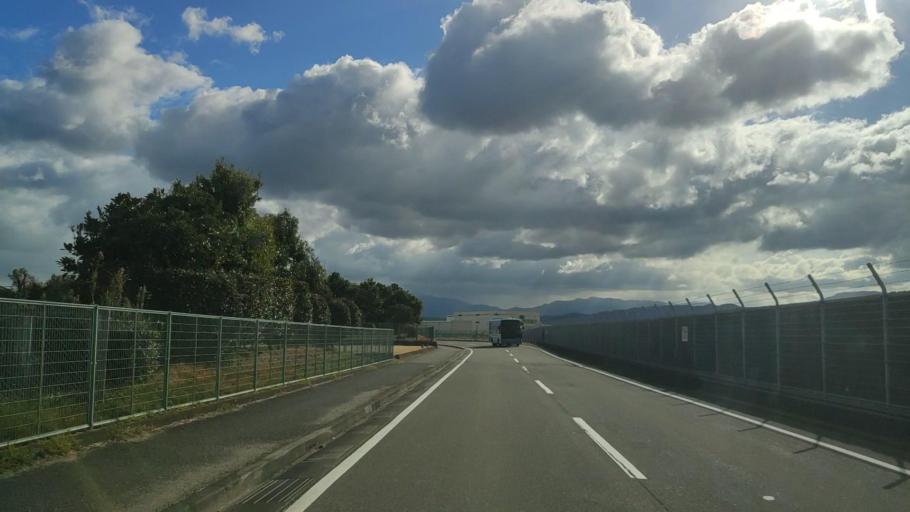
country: JP
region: Ehime
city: Masaki-cho
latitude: 33.8228
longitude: 132.7100
